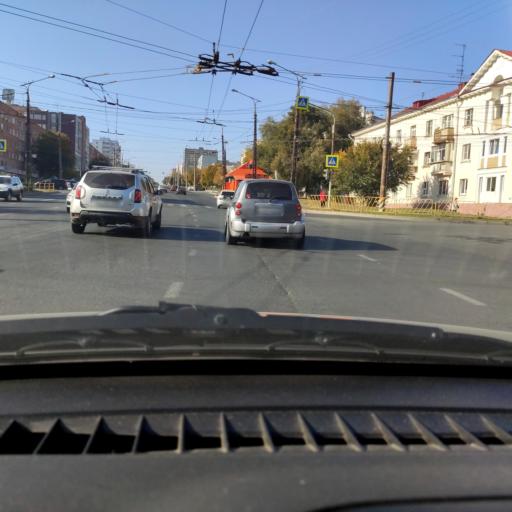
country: RU
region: Samara
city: Zhigulevsk
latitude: 53.4742
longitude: 49.4733
